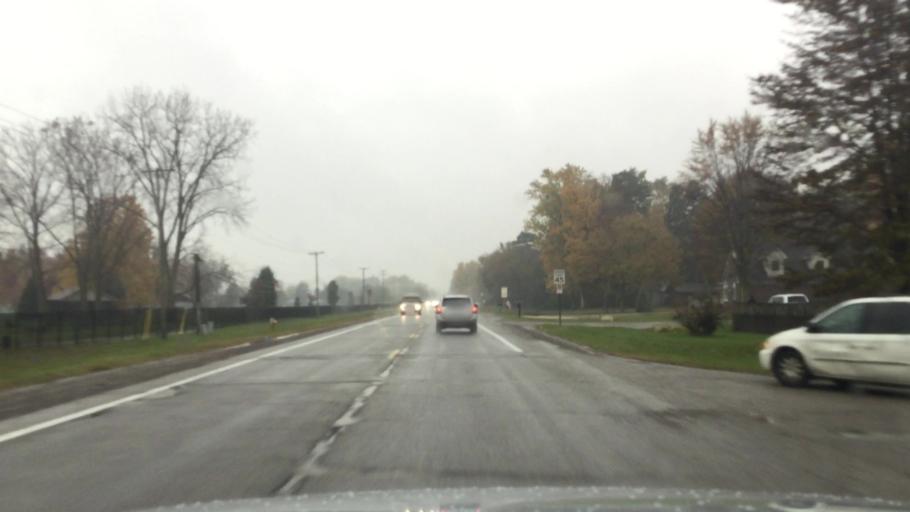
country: US
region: Michigan
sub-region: Macomb County
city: New Baltimore
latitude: 42.6691
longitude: -82.7573
